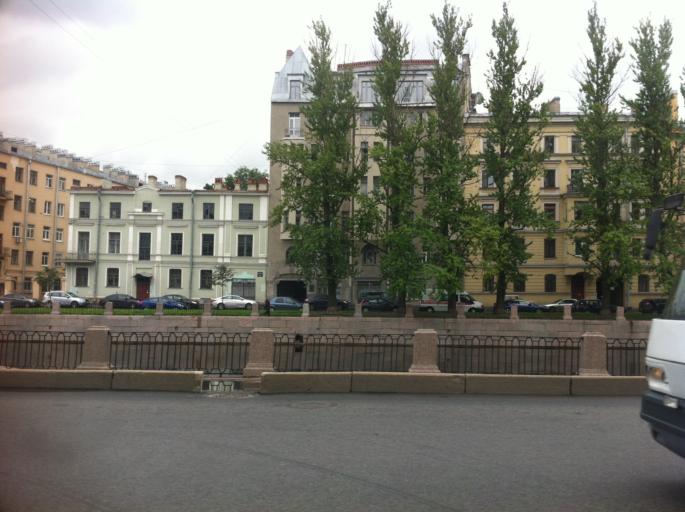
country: RU
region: St.-Petersburg
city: Admiralteisky
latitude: 59.9204
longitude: 30.2858
